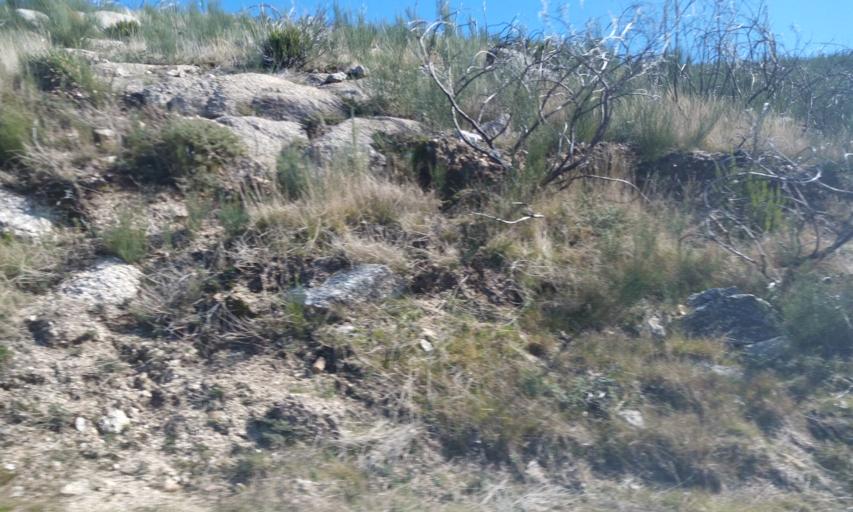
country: PT
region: Guarda
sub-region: Manteigas
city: Manteigas
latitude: 40.4896
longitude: -7.5503
